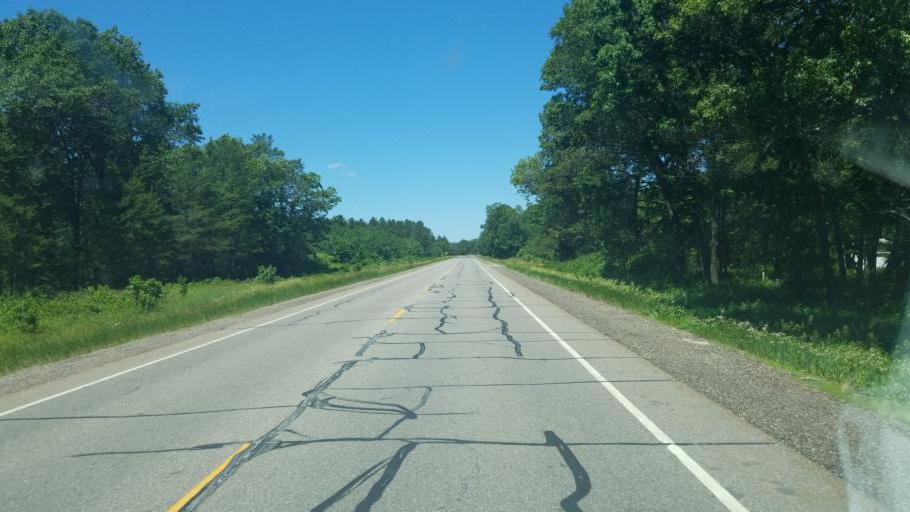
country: US
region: Wisconsin
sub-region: Adams County
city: Friendship
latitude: 44.0428
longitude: -89.9646
